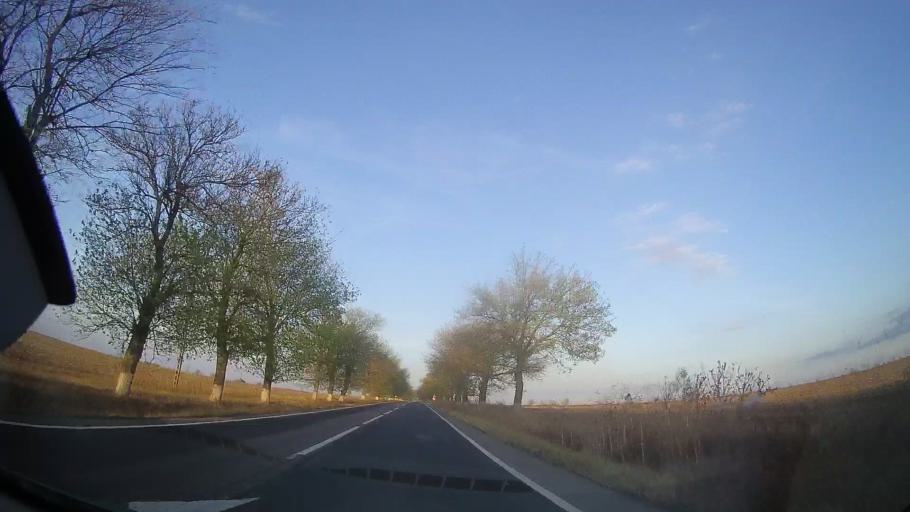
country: RO
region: Constanta
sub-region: Comuna Comana
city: Comana
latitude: 43.8988
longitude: 28.3229
